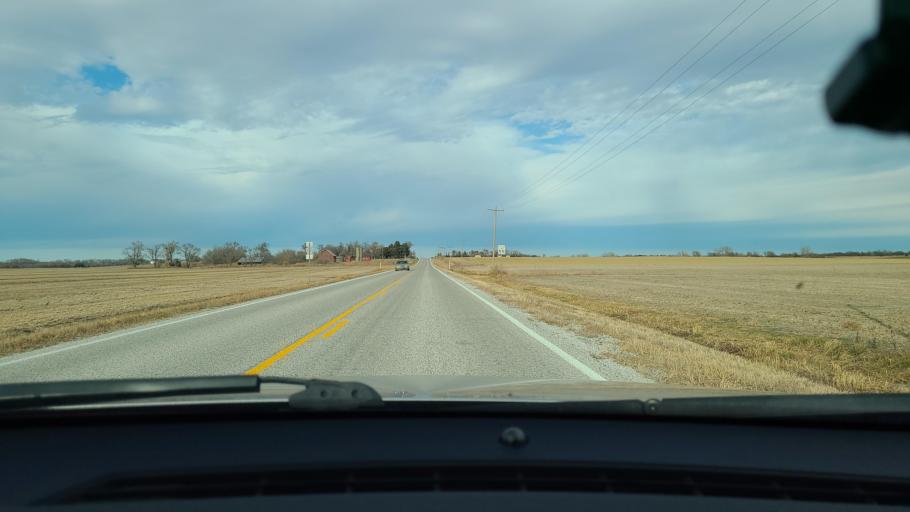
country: US
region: Kansas
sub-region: McPherson County
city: Inman
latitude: 38.2904
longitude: -97.9250
